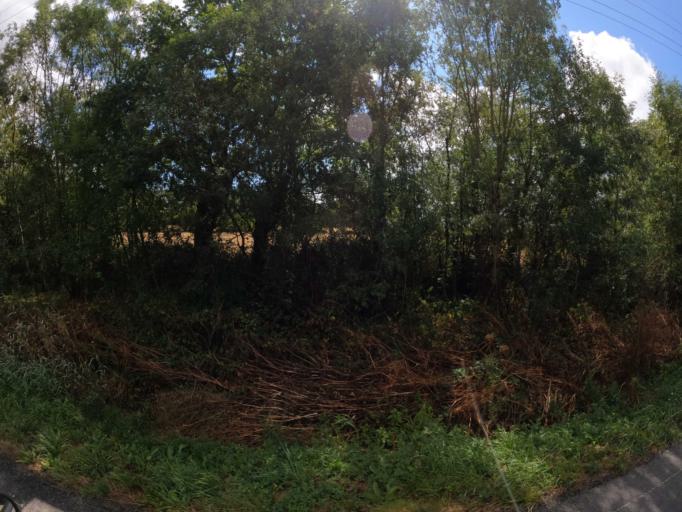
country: FR
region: Pays de la Loire
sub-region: Departement de la Loire-Atlantique
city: Vallet
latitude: 47.1861
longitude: -1.2551
